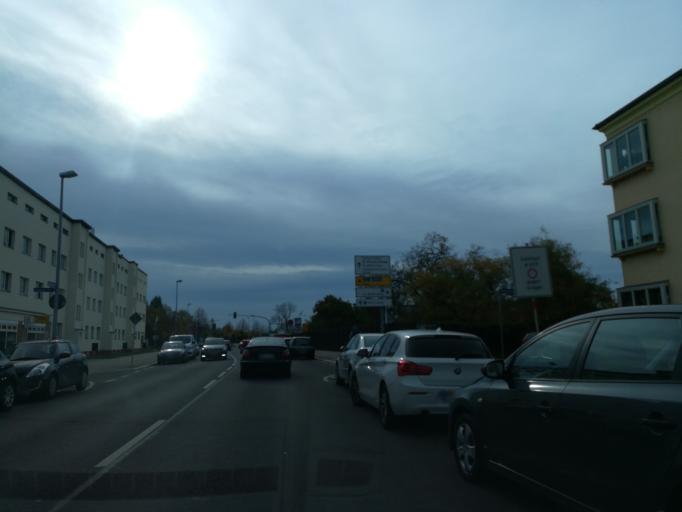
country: DE
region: Saxony-Anhalt
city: Magdeburg
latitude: 52.1302
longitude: 11.6673
